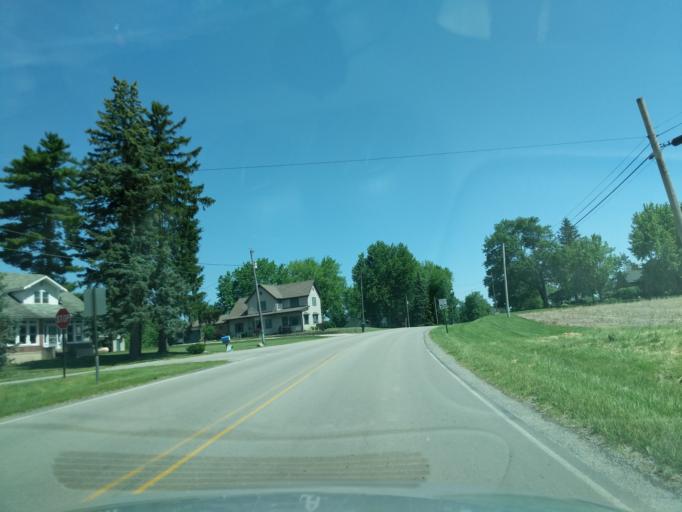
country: US
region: Indiana
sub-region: Huntington County
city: Huntington
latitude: 40.8969
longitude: -85.4844
